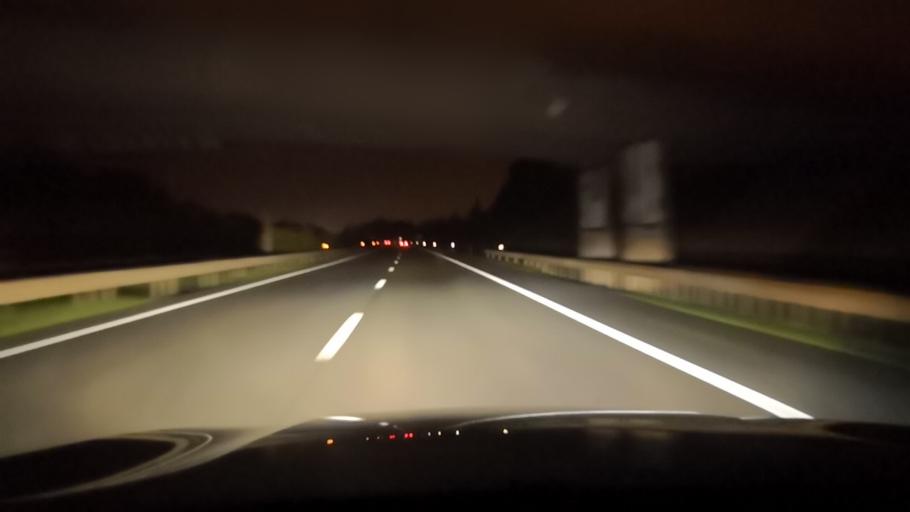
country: PT
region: Setubal
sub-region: Setubal
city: Setubal
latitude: 38.5529
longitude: -8.8709
